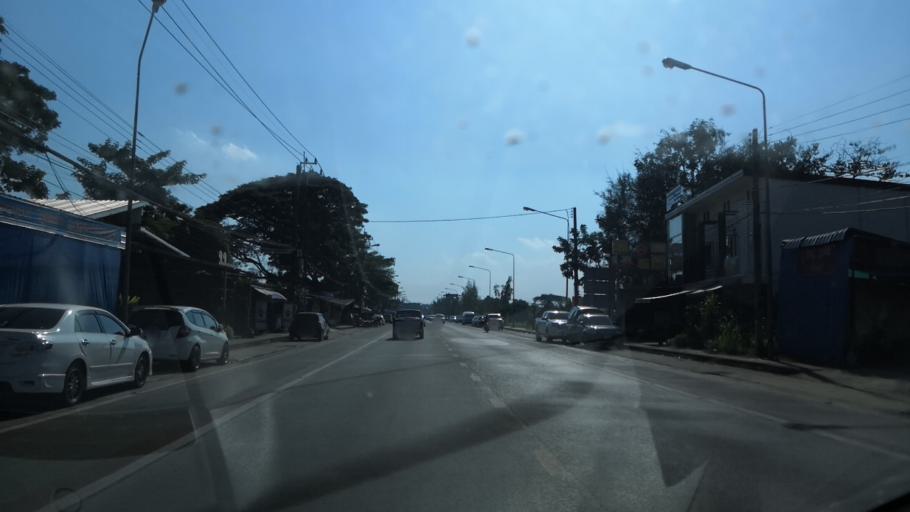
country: TH
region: Chiang Rai
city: Chiang Rai
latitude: 19.9328
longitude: 99.8407
